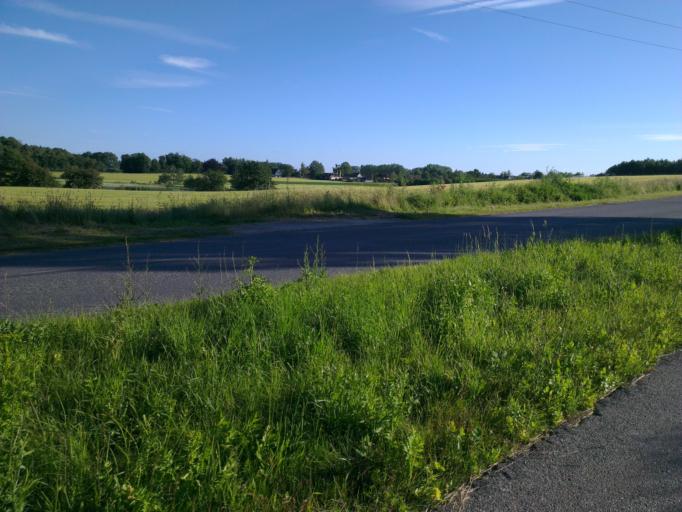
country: DK
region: Capital Region
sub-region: Frederikssund Kommune
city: Jaegerspris
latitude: 55.8224
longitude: 12.0103
